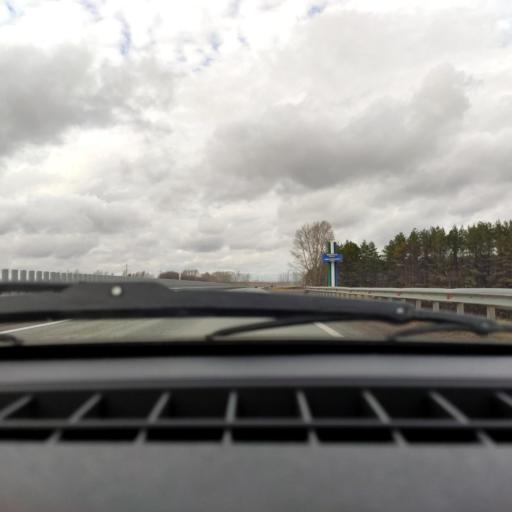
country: RU
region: Bashkortostan
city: Asanovo
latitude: 54.9189
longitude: 55.5851
